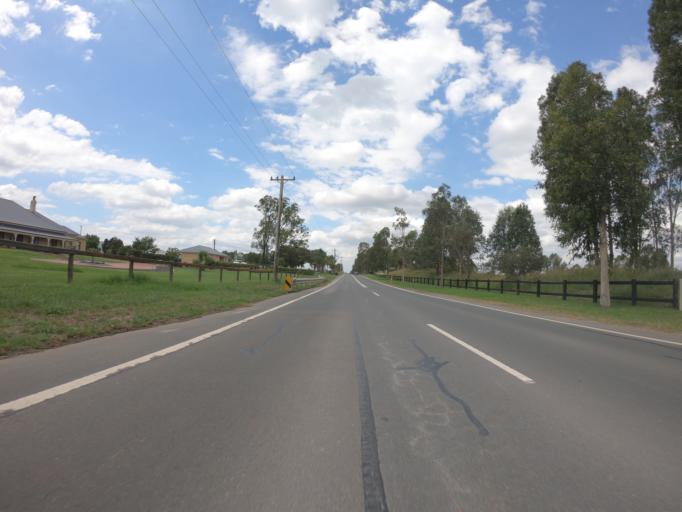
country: AU
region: New South Wales
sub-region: Liverpool
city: Luddenham
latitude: -33.8363
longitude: 150.7512
